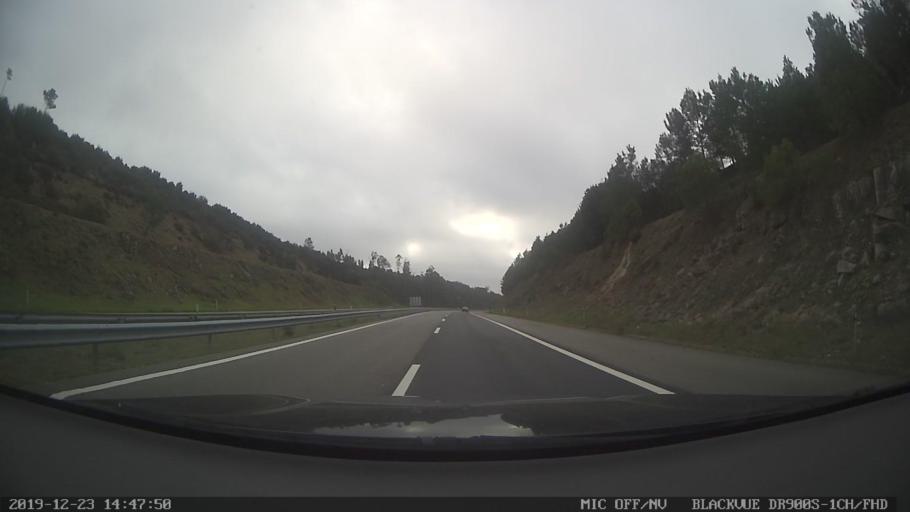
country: PT
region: Viseu
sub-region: Castro Daire
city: Castro Daire
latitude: 40.8797
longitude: -7.9213
